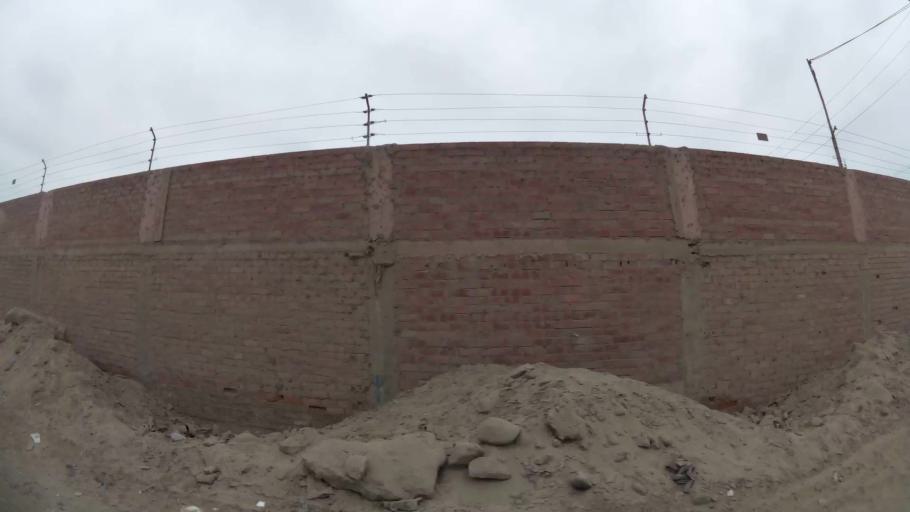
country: PE
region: Lima
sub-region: Lima
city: Surco
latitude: -12.2126
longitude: -76.9683
